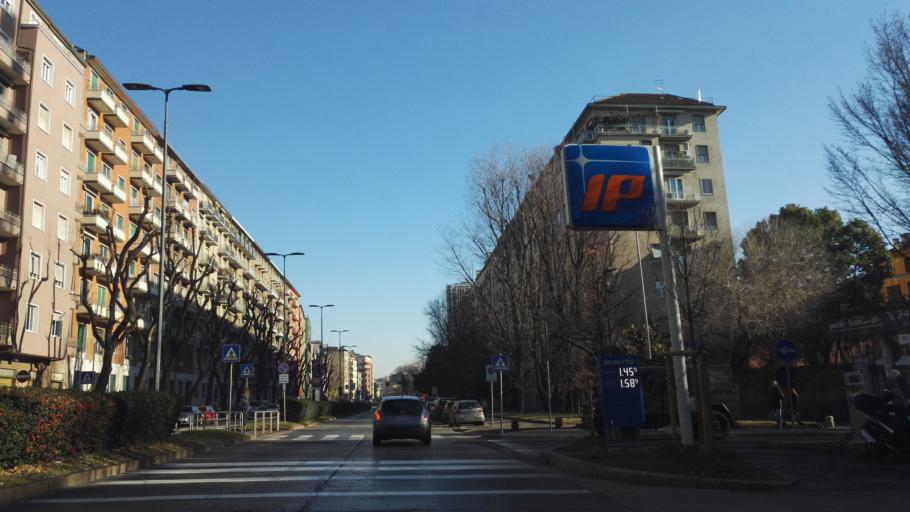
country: IT
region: Lombardy
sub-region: Citta metropolitana di Milano
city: Milano
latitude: 45.4519
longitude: 9.1938
